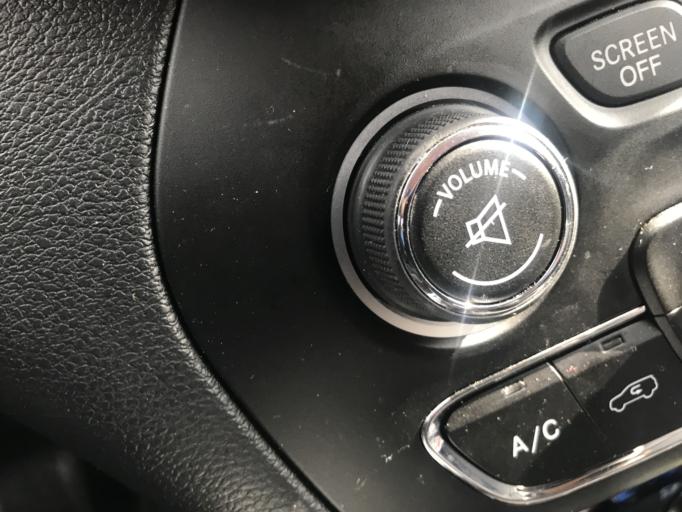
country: US
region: Colorado
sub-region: Arapahoe County
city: Columbine Valley
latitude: 39.5657
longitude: -105.0150
